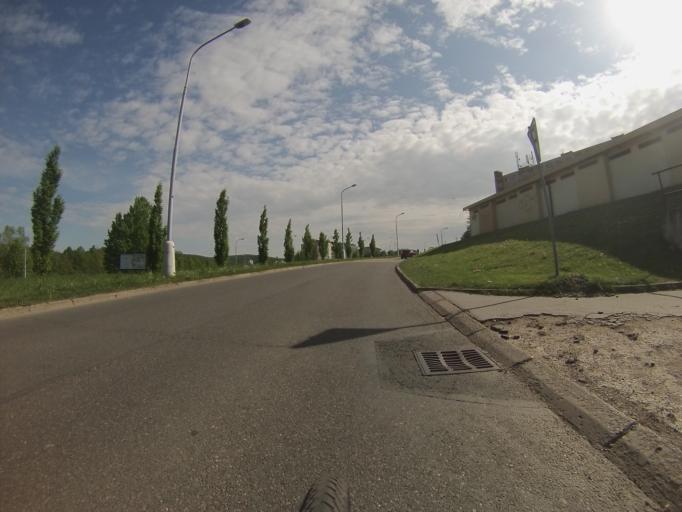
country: CZ
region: South Moravian
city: Troubsko
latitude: 49.2195
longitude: 16.5195
